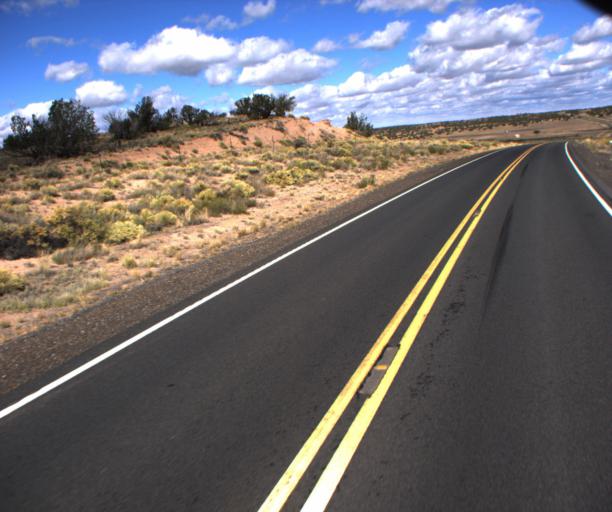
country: US
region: Arizona
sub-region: Apache County
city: Houck
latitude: 35.0880
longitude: -109.3107
